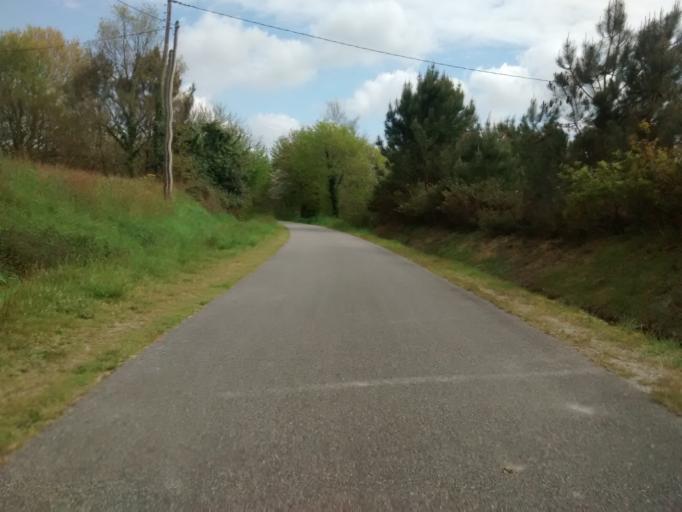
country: FR
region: Brittany
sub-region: Departement du Morbihan
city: Malestroit
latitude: 47.7909
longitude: -2.4045
